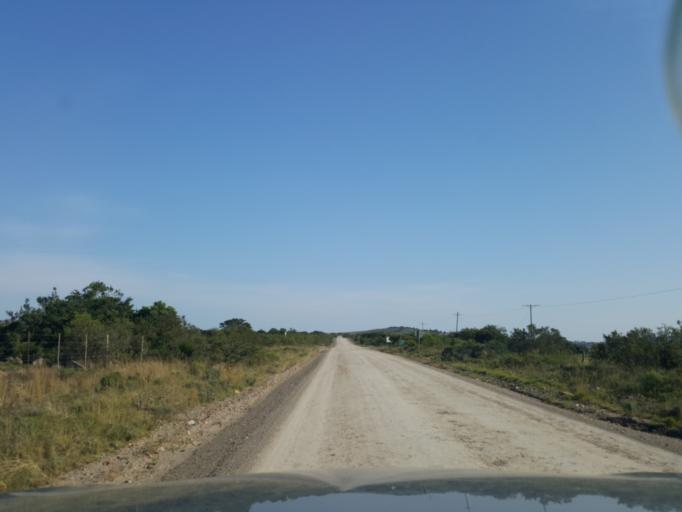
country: ZA
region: Eastern Cape
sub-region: Cacadu District Municipality
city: Grahamstown
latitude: -33.3810
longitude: 26.3004
